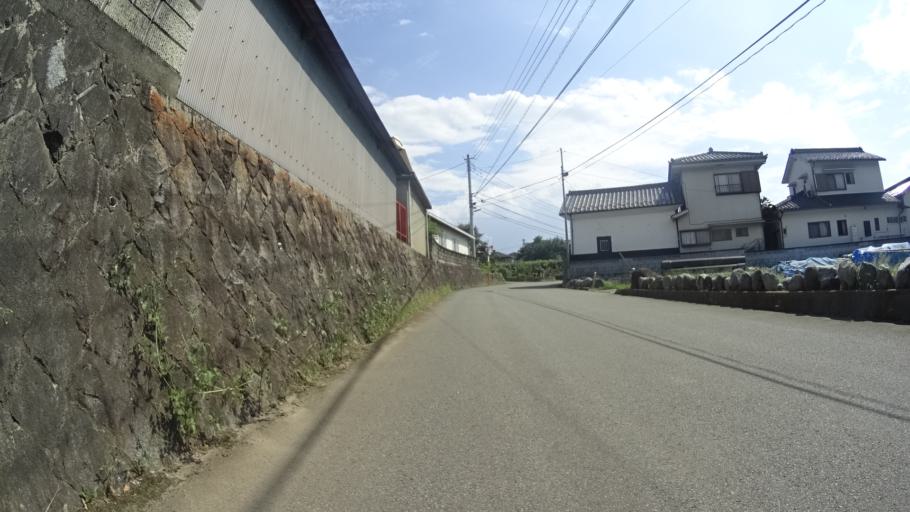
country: JP
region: Yamanashi
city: Enzan
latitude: 35.7168
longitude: 138.7337
